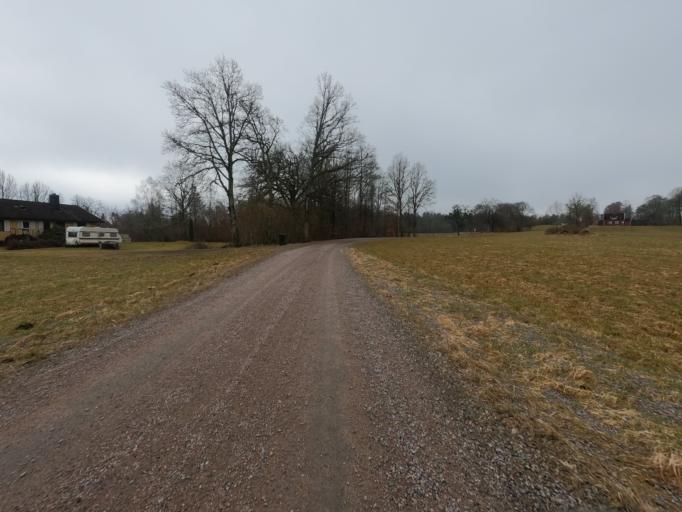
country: SE
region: Kronoberg
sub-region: Markaryds Kommun
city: Stromsnasbruk
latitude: 56.8236
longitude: 13.5631
